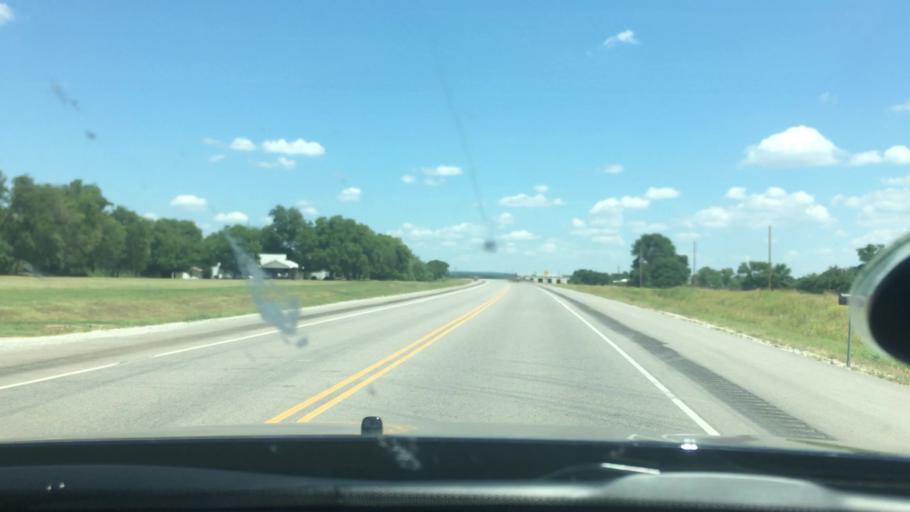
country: US
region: Oklahoma
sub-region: Carter County
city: Dickson
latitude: 34.2306
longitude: -96.9765
